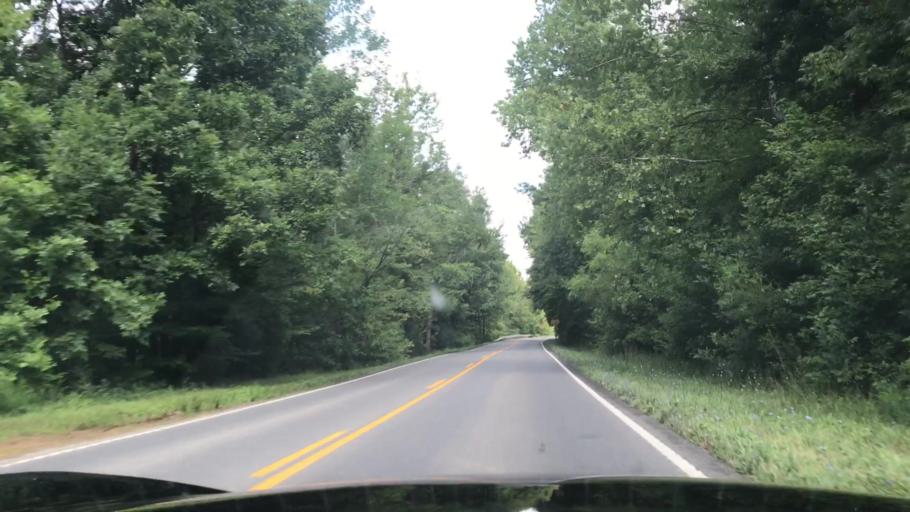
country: US
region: Kentucky
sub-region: Muhlenberg County
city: Central City
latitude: 37.2108
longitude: -87.0430
